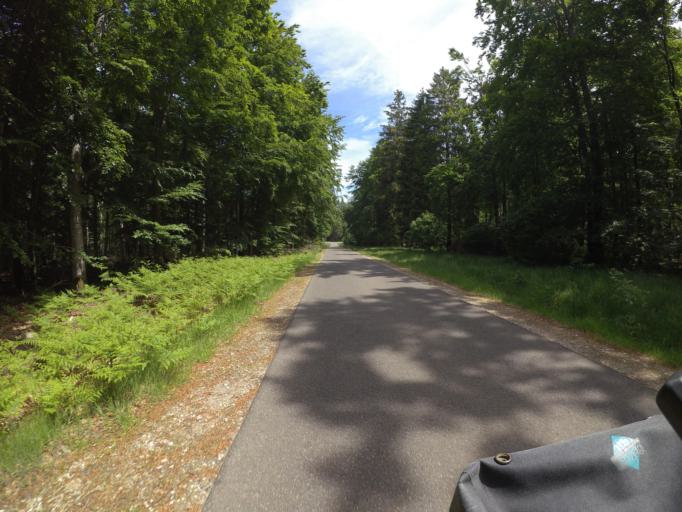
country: DE
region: Rheinland-Pfalz
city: Borfink
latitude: 49.7086
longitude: 7.0681
